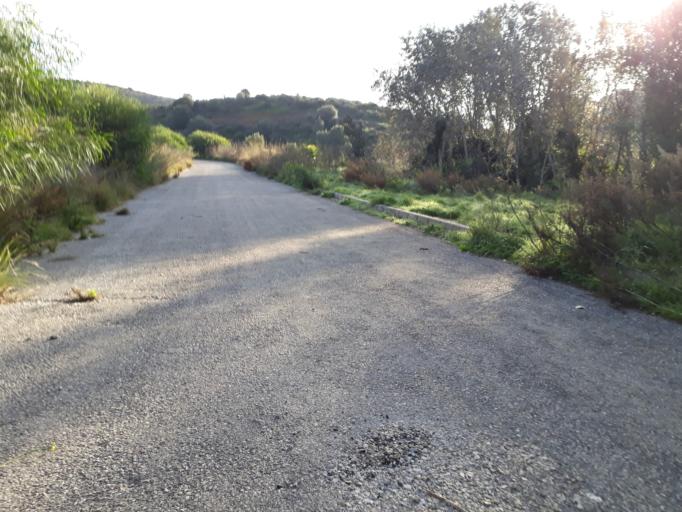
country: ES
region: Andalusia
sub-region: Provincia de Malaga
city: Fuengirola
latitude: 36.5031
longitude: -4.6996
